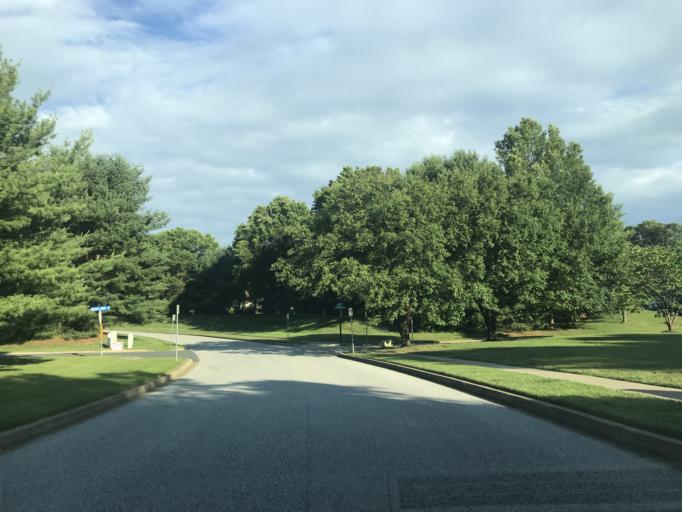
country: US
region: Maryland
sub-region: Harford County
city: South Bel Air
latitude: 39.5610
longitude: -76.3253
